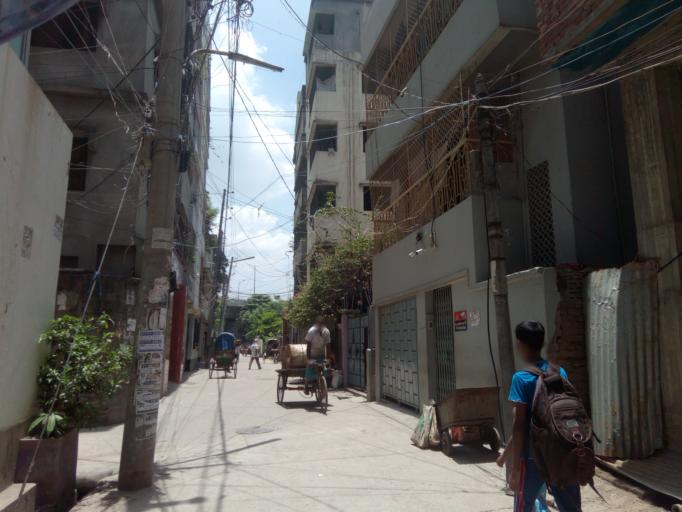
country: BD
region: Dhaka
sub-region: Dhaka
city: Dhaka
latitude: 23.7158
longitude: 90.4243
